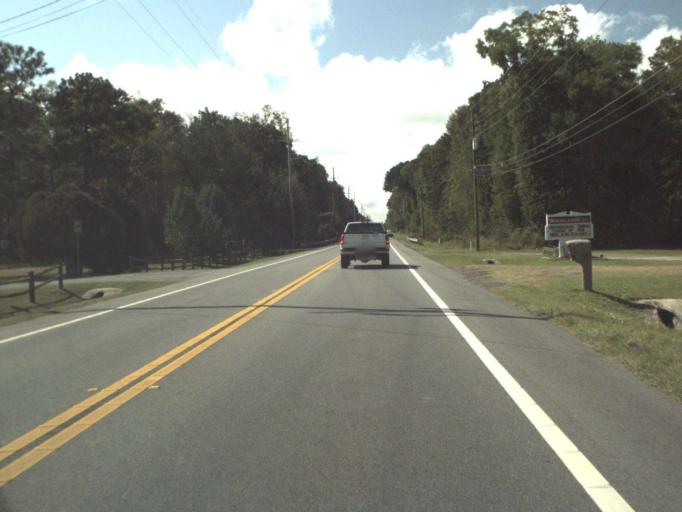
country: US
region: Florida
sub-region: Gadsden County
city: Midway
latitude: 30.4264
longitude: -84.5350
